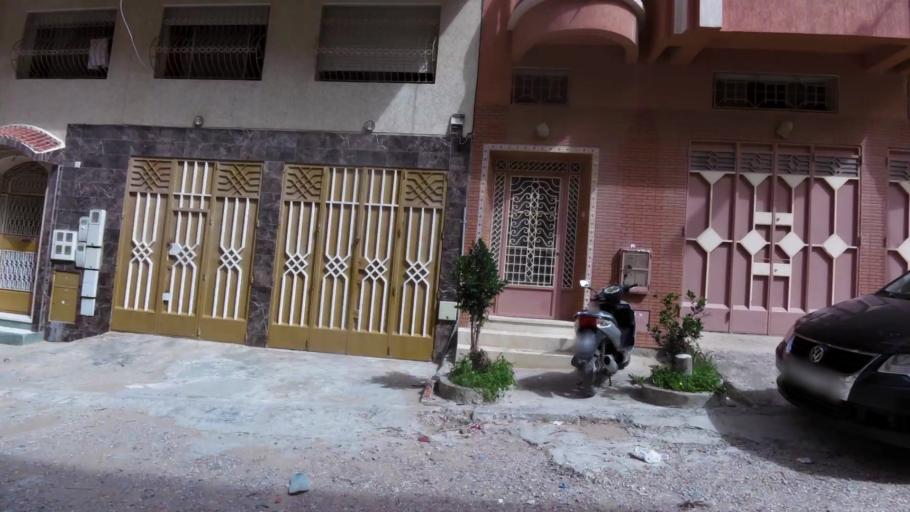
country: MA
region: Tanger-Tetouan
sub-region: Tanger-Assilah
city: Tangier
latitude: 35.7406
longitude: -5.8358
